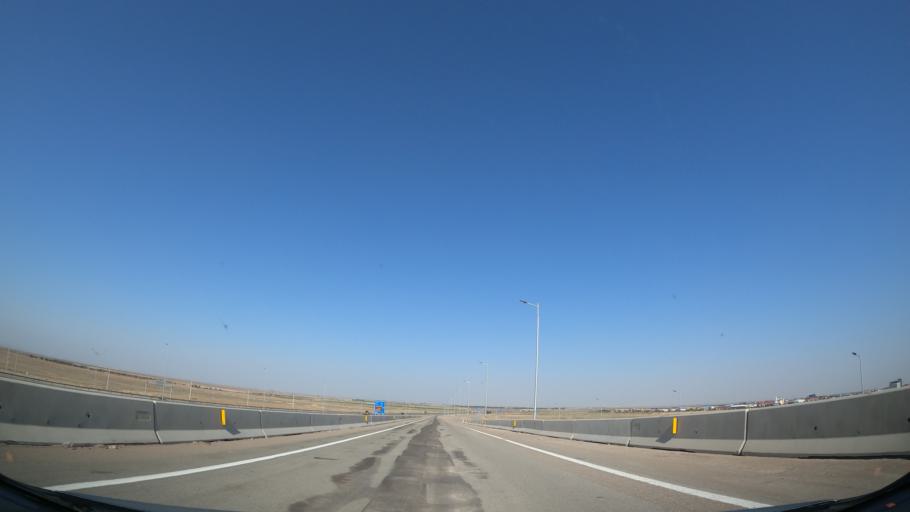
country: IR
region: Tehran
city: Eqbaliyeh
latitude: 35.1343
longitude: 51.5182
